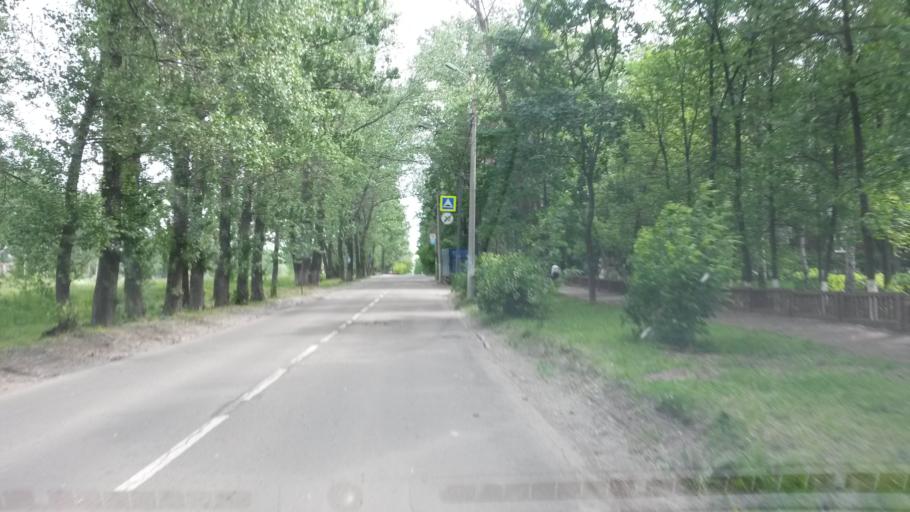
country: RU
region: Jaroslavl
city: Yaroslavl
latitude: 57.5886
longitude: 39.8344
